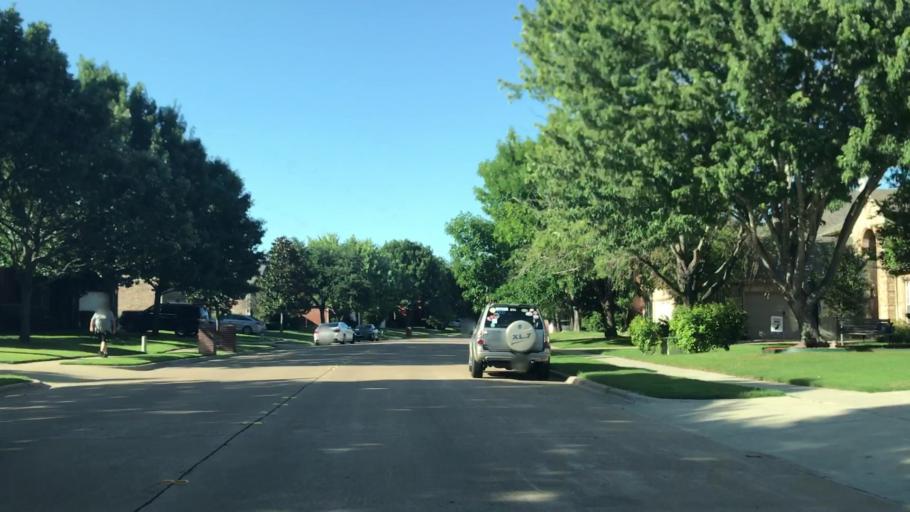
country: US
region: Texas
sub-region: Collin County
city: Frisco
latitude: 33.1188
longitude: -96.7808
